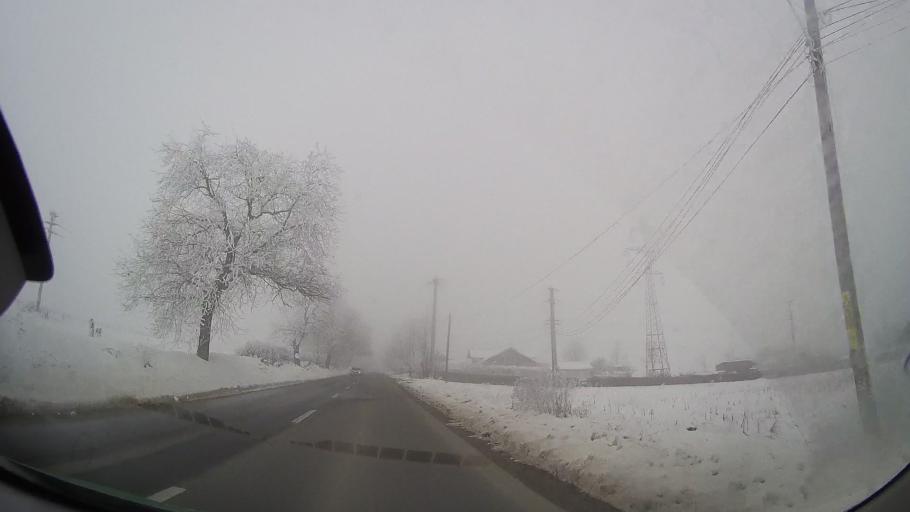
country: RO
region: Iasi
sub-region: Comuna Valea Seaca
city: Valea Seaca
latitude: 47.2913
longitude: 26.6760
